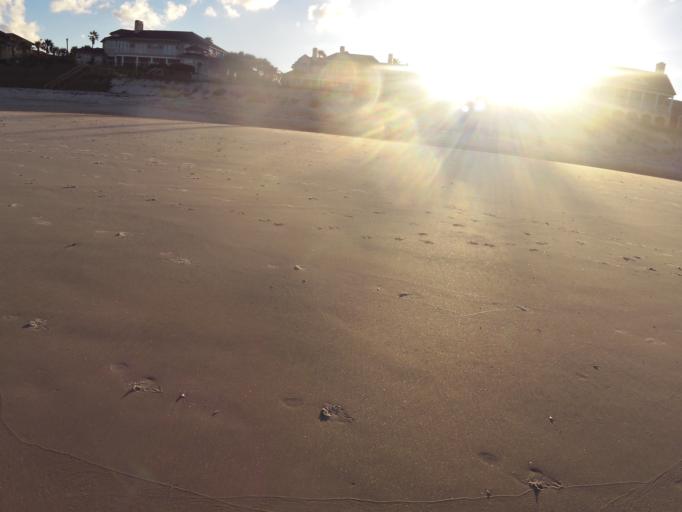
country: US
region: Florida
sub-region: Saint Johns County
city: Sawgrass
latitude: 30.1716
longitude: -81.3580
